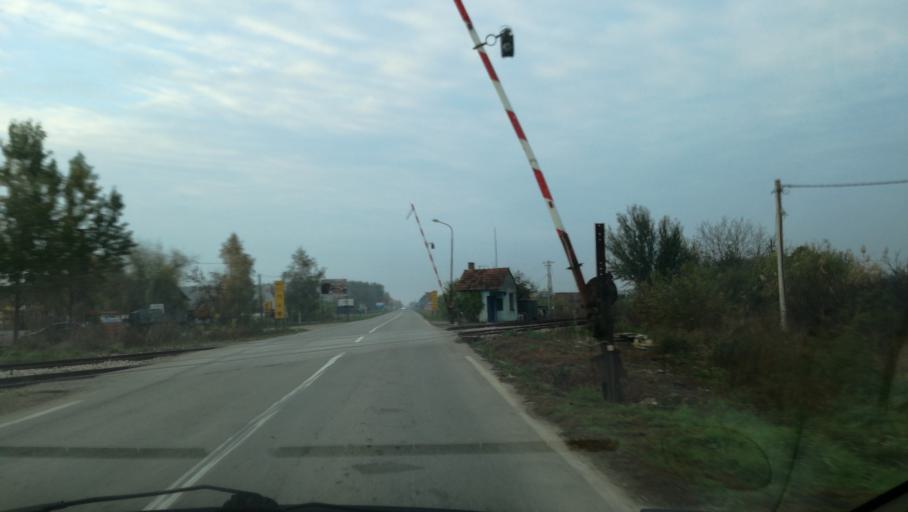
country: RS
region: Autonomna Pokrajina Vojvodina
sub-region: Severnobanatski Okrug
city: Kikinda
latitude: 45.7949
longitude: 20.4380
